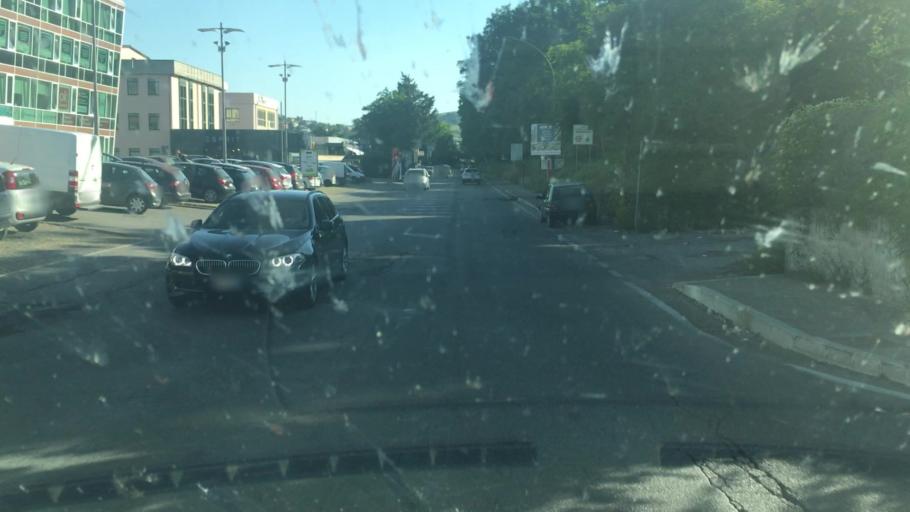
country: IT
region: Basilicate
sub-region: Provincia di Potenza
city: Potenza
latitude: 40.6330
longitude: 15.8127
